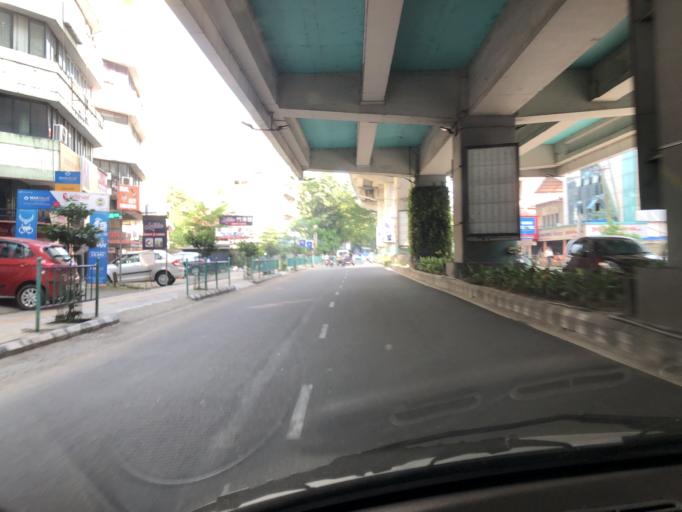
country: IN
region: Kerala
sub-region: Ernakulam
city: Elur
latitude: 10.0152
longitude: 76.3024
